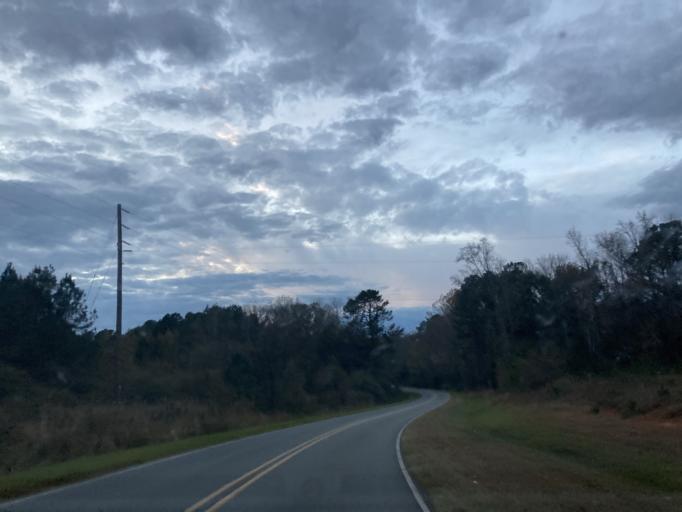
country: US
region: Georgia
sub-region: Jones County
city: Gray
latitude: 32.9731
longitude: -83.5044
